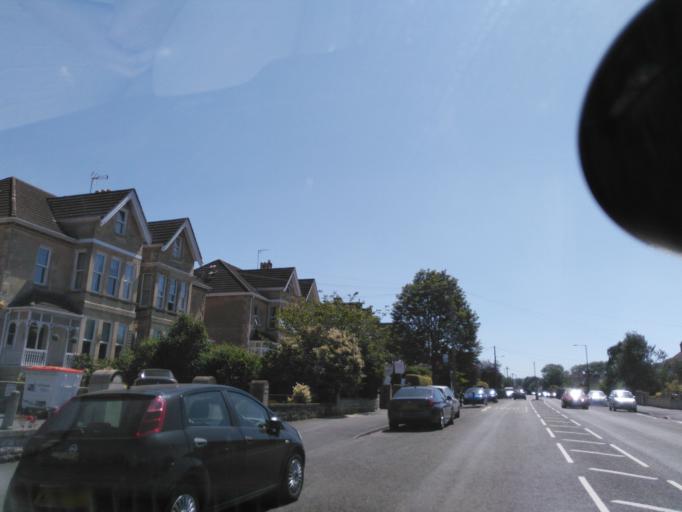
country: GB
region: England
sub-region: Bath and North East Somerset
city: Bath
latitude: 51.3871
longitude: -2.3991
